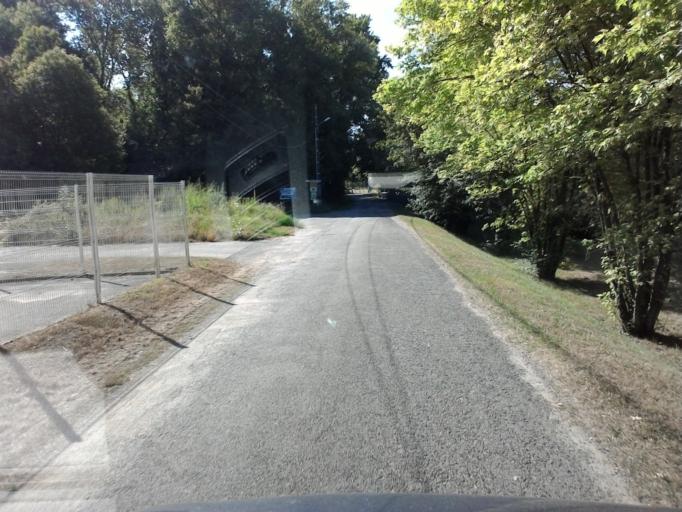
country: FR
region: Rhone-Alpes
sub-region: Departement de l'Ain
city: Sault-Brenaz
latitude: 45.8524
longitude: 5.4091
